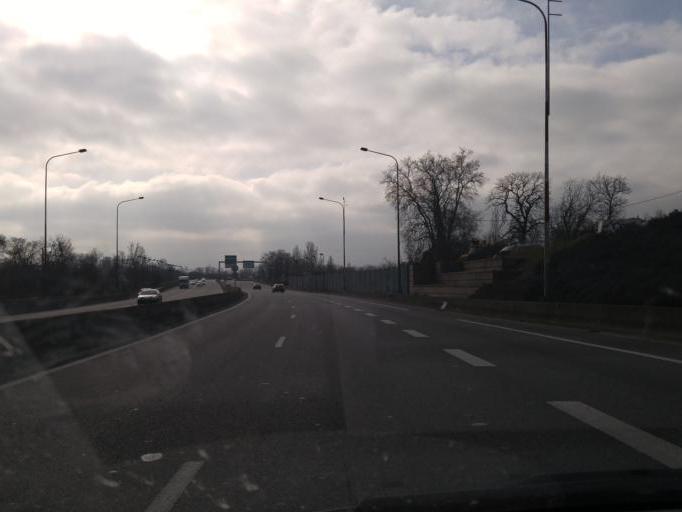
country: FR
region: Midi-Pyrenees
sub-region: Departement de la Haute-Garonne
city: Blagnac
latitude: 43.6142
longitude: 1.3872
